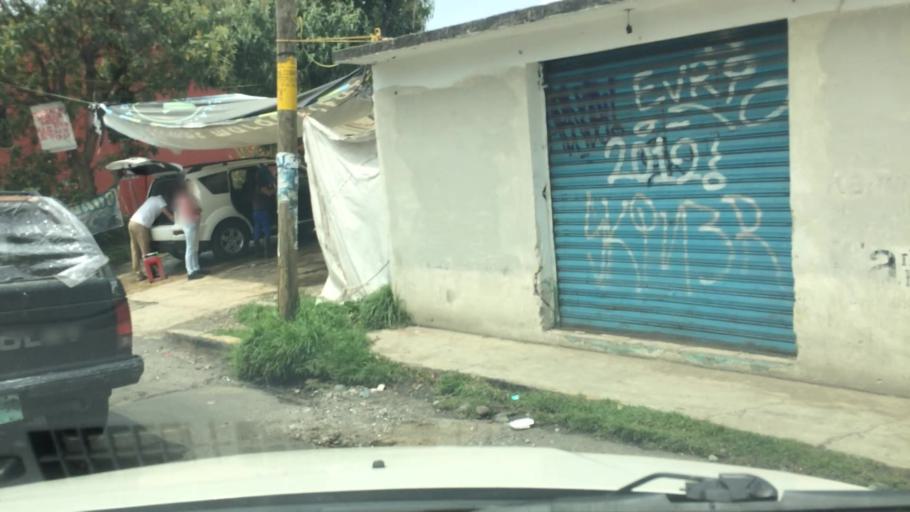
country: MX
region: Mexico City
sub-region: Tlalpan
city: Lomas de Tepemecatl
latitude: 19.2244
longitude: -99.2042
